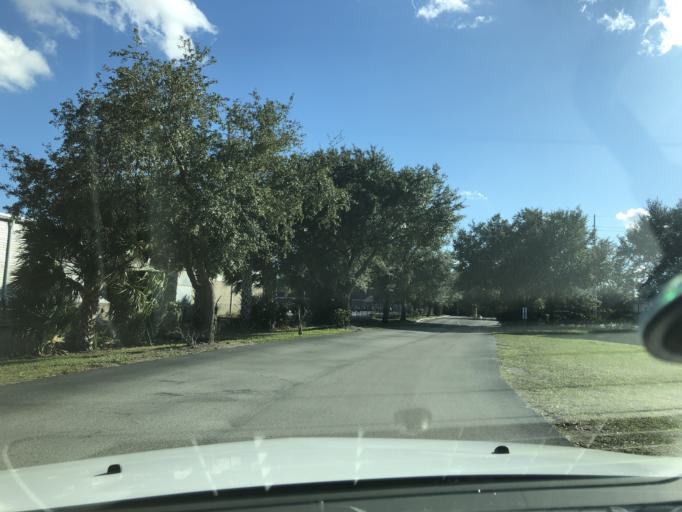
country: US
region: Florida
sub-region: Orange County
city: Oak Ridge
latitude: 28.4738
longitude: -81.4292
